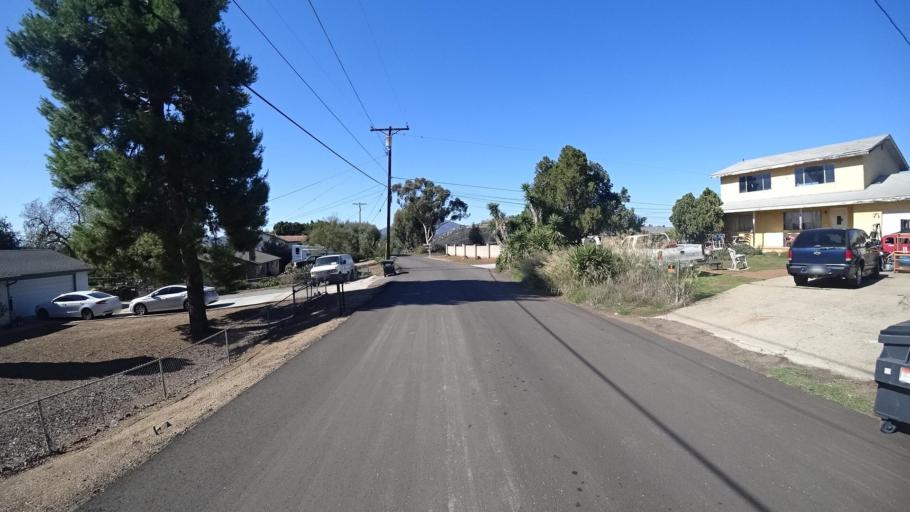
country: US
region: California
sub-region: San Diego County
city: Jamul
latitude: 32.7279
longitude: -116.8677
